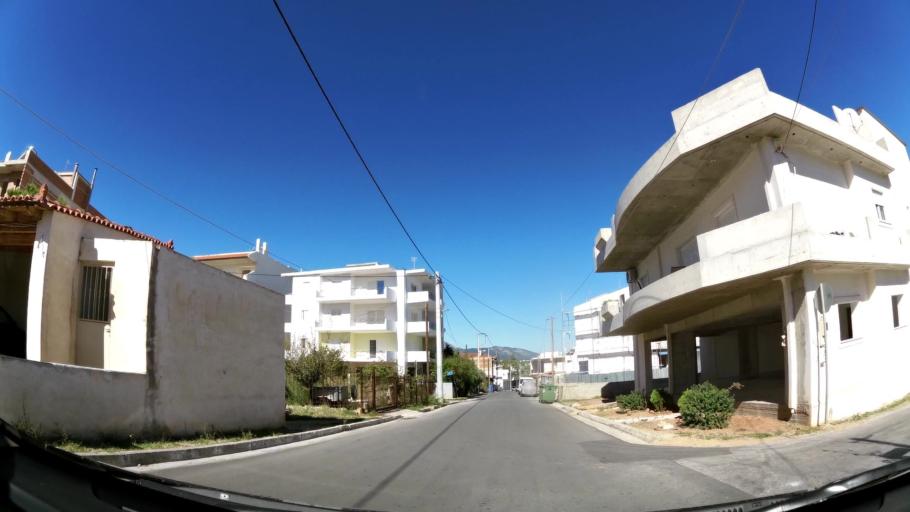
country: GR
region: Attica
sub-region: Nomarchia Anatolikis Attikis
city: Koropi
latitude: 37.9040
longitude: 23.8806
